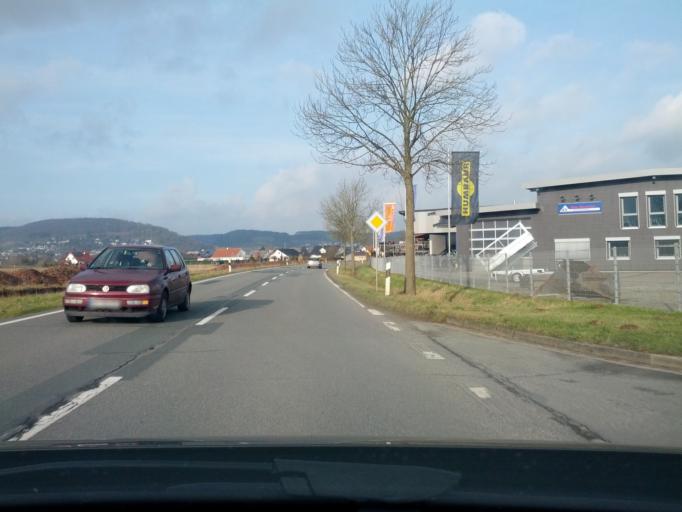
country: DE
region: North Rhine-Westphalia
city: Beverungen
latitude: 51.6526
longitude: 9.3883
